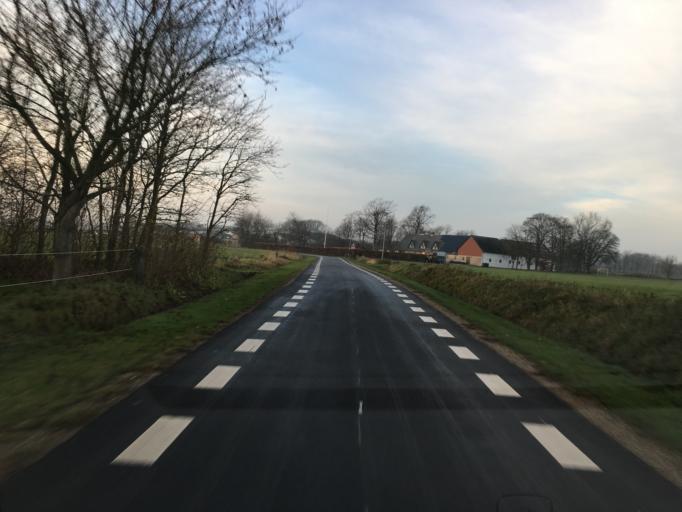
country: DK
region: South Denmark
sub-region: Tonder Kommune
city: Toftlund
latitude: 55.1255
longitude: 9.0677
